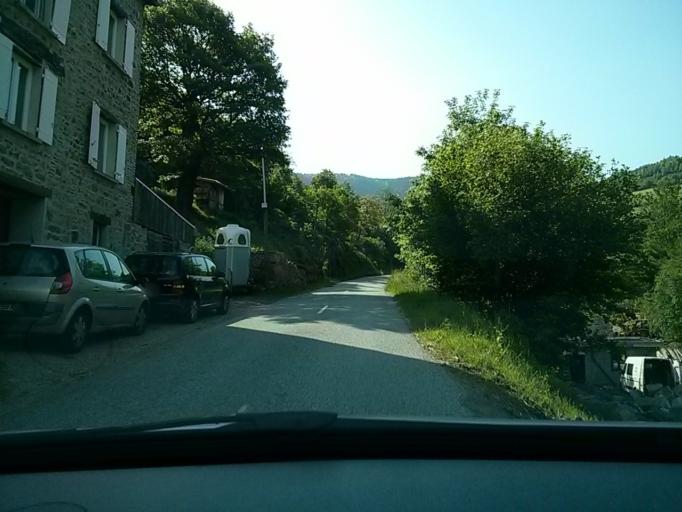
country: FR
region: Rhone-Alpes
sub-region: Departement de la Loire
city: Saint-Chamond
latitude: 45.4070
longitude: 4.5404
